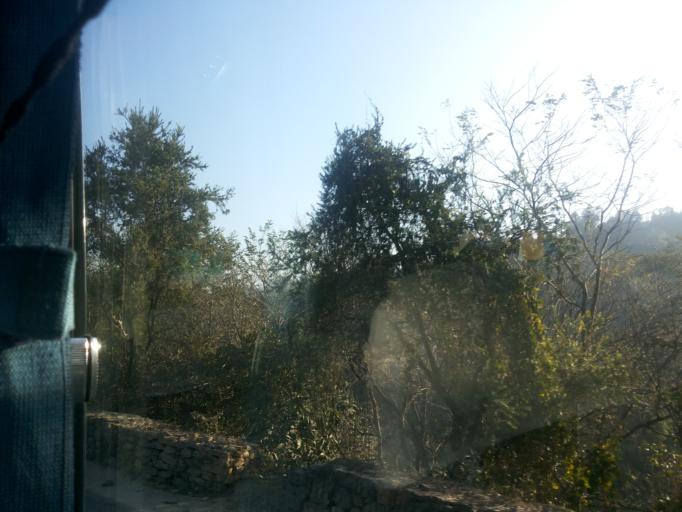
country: NP
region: Central Region
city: Kirtipur
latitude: 27.7133
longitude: 85.1804
